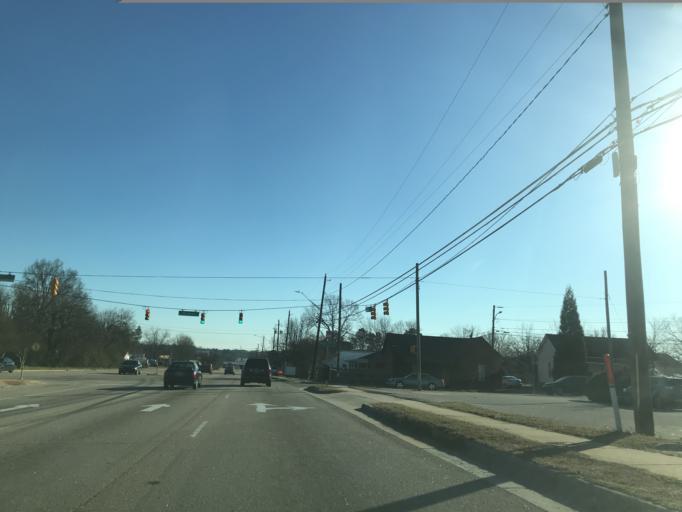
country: US
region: North Carolina
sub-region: Wake County
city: Raleigh
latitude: 35.7614
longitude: -78.6493
